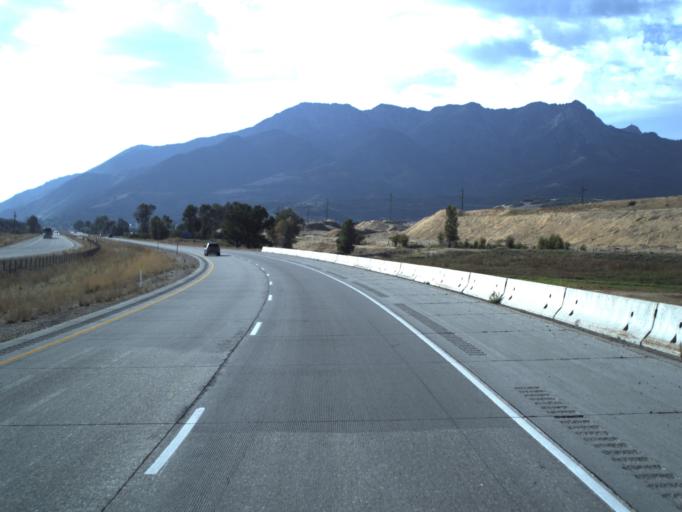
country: US
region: Utah
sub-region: Morgan County
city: Mountain Green
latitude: 41.1365
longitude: -111.7873
